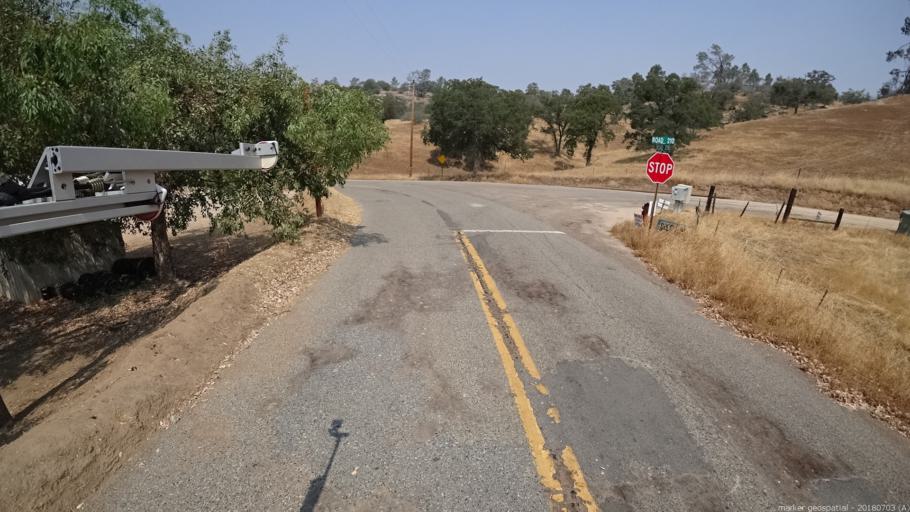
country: US
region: California
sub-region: Madera County
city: Yosemite Lakes
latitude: 37.0666
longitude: -119.6734
